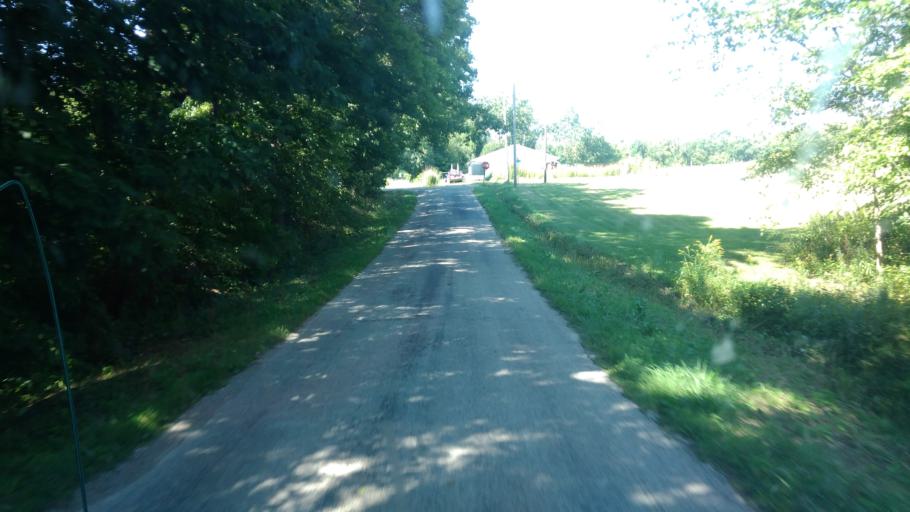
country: US
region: Ohio
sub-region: Ashland County
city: Ashland
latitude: 40.9370
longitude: -82.2626
